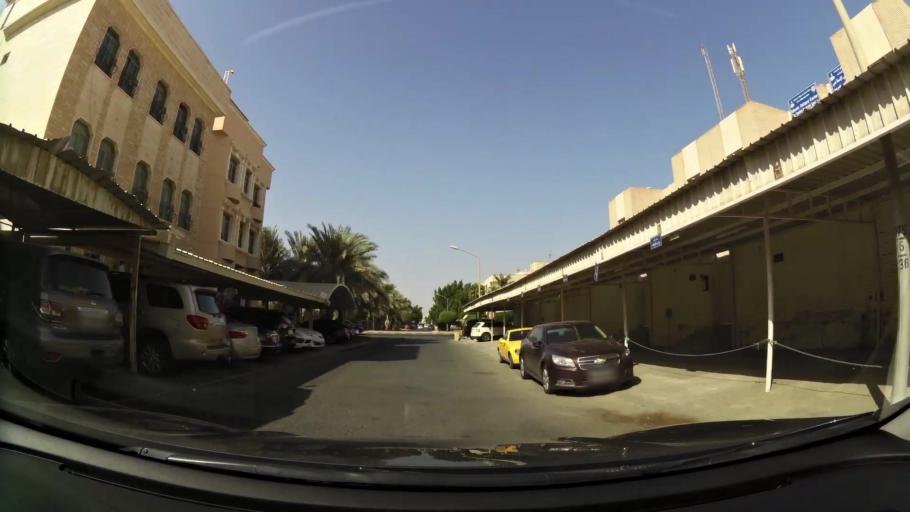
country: KW
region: Muhafazat Hawalli
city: Salwa
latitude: 29.2858
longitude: 48.0856
